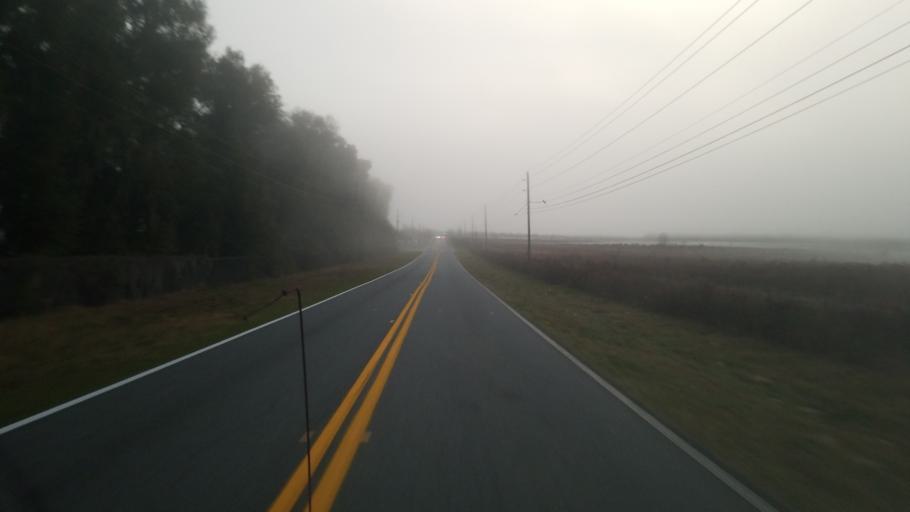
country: US
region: Florida
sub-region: Marion County
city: Ocala
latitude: 29.1502
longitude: -82.2291
